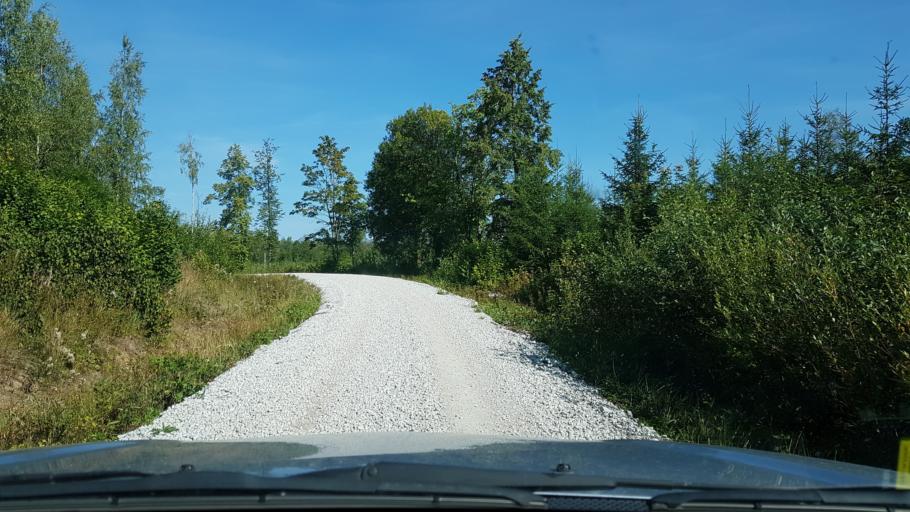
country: EE
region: Ida-Virumaa
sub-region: Sillamaee linn
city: Sillamae
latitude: 59.3336
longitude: 27.7328
